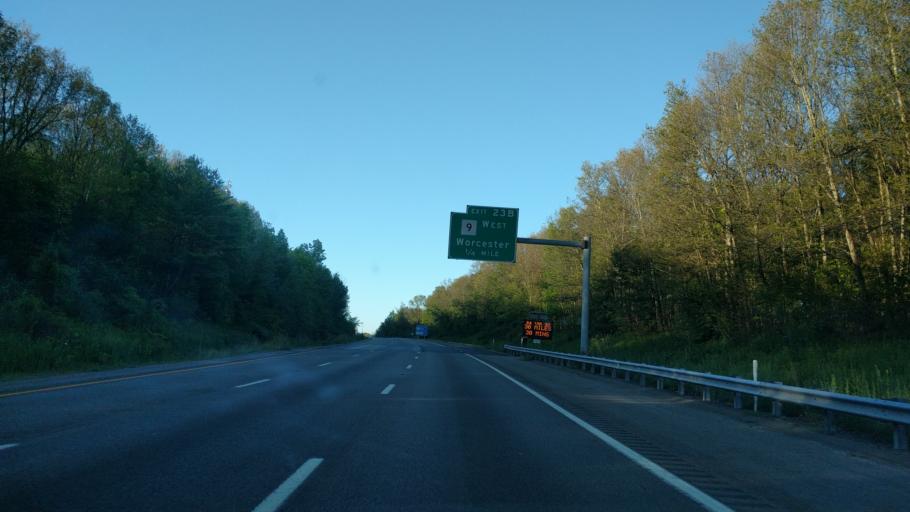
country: US
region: Massachusetts
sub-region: Worcester County
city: Southborough
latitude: 42.2964
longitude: -71.5676
